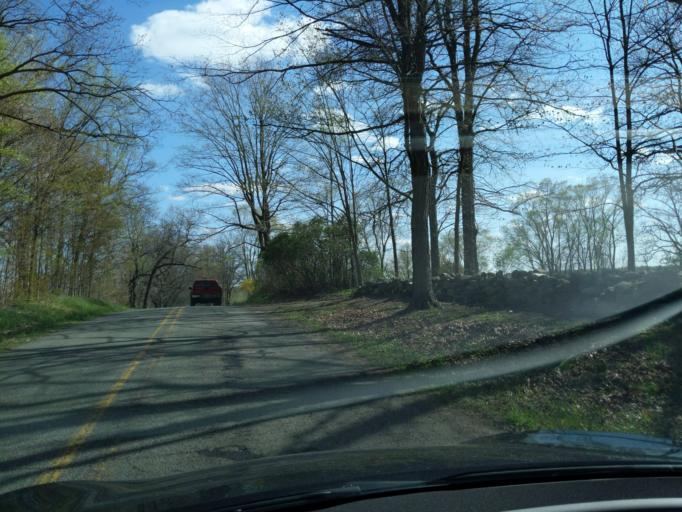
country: US
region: Michigan
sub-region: Ingham County
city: Leslie
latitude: 42.3553
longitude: -84.5318
